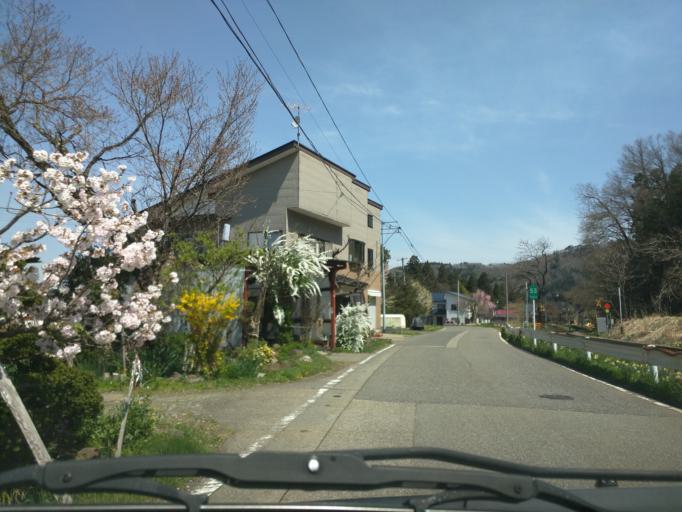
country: JP
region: Fukushima
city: Kitakata
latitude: 37.5240
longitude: 139.7225
